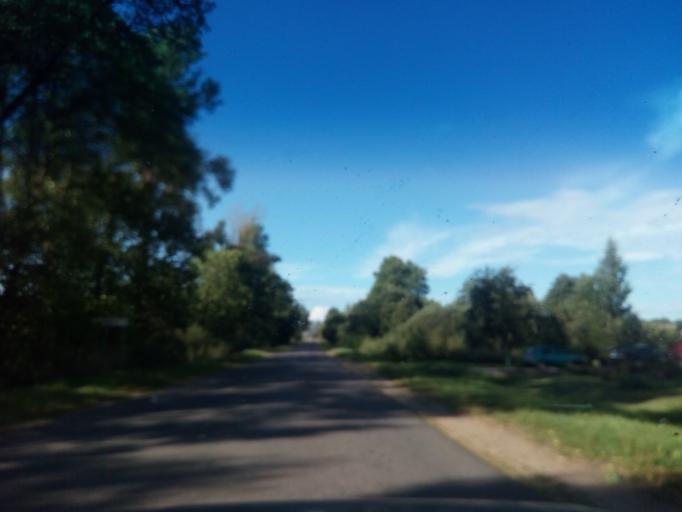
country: BY
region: Vitebsk
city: Dzisna
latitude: 55.6627
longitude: 28.3253
